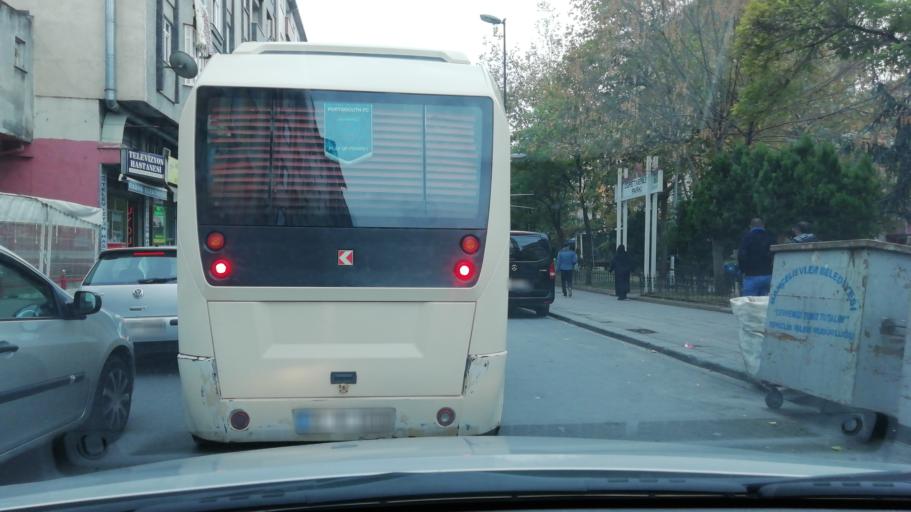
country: TR
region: Istanbul
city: Bahcelievler
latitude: 41.0031
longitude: 28.8388
